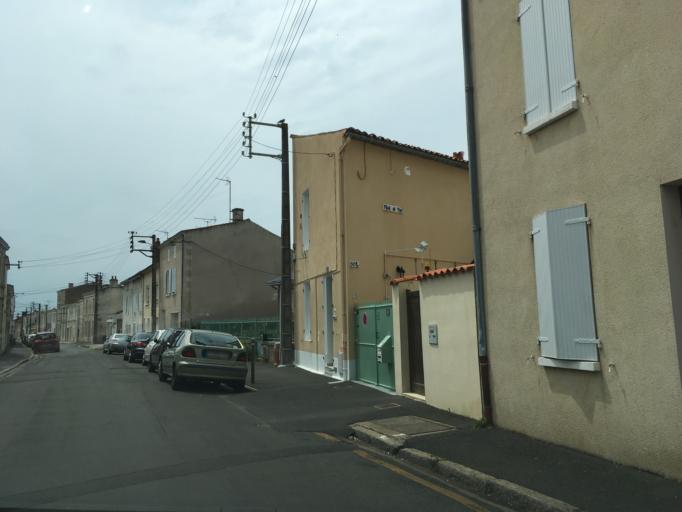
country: FR
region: Poitou-Charentes
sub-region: Departement des Deux-Sevres
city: Niort
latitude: 46.3214
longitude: -0.4709
